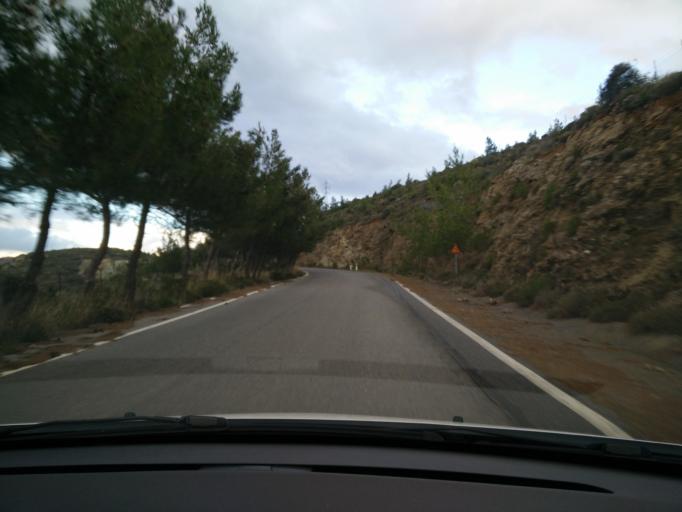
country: GR
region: Crete
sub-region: Nomos Lasithiou
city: Gra Liyia
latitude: 35.0889
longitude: 25.6994
